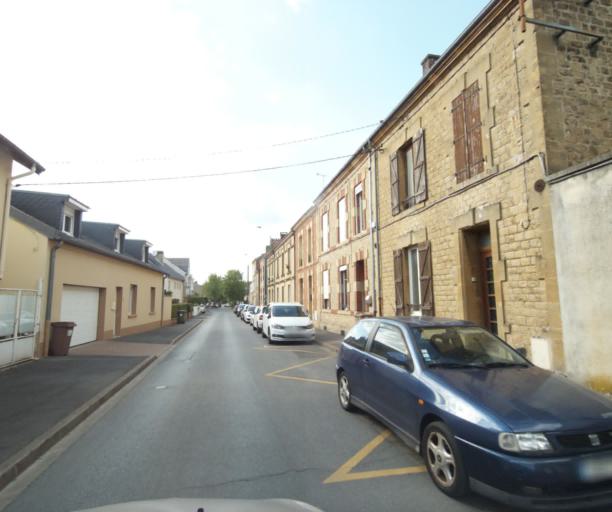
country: FR
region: Champagne-Ardenne
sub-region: Departement des Ardennes
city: Montcy-Notre-Dame
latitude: 49.7774
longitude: 4.7334
